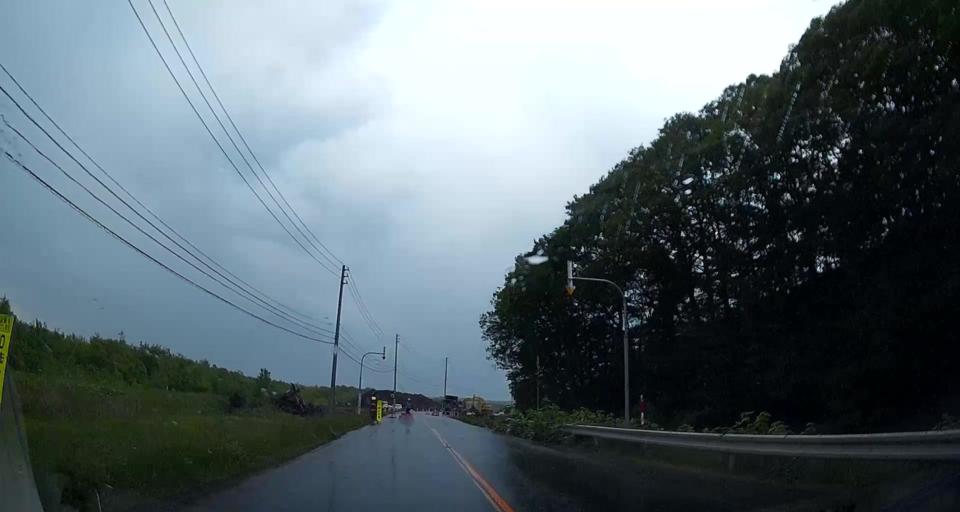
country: JP
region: Hokkaido
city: Chitose
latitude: 42.7379
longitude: 141.9024
